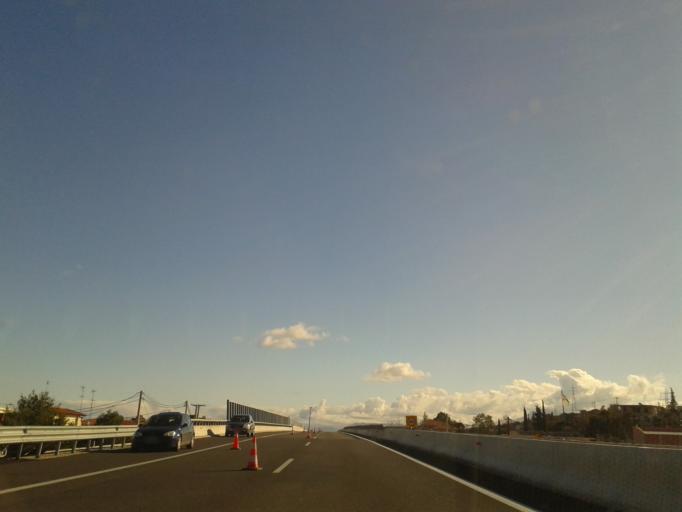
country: GR
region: West Greece
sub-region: Nomos Achaias
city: Kamarai
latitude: 38.2993
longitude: 21.9996
